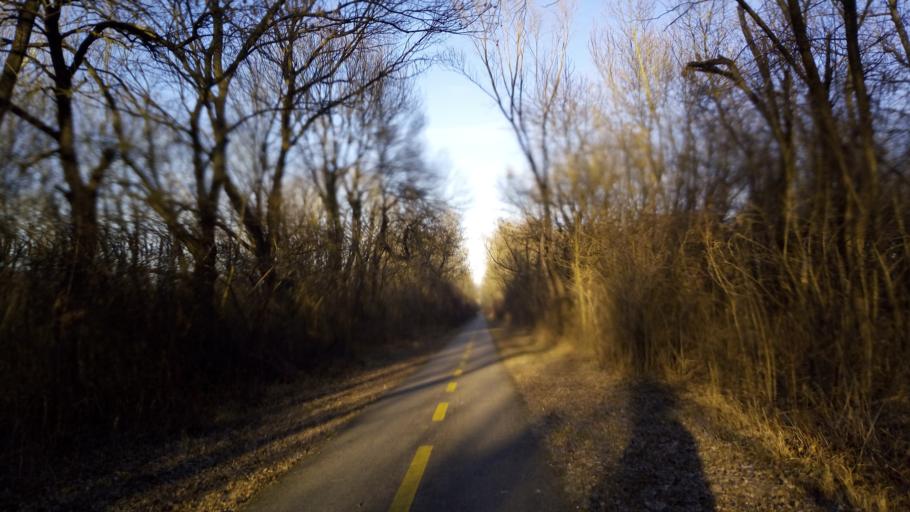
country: HU
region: Baranya
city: Pellerd
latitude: 46.0406
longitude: 18.1784
